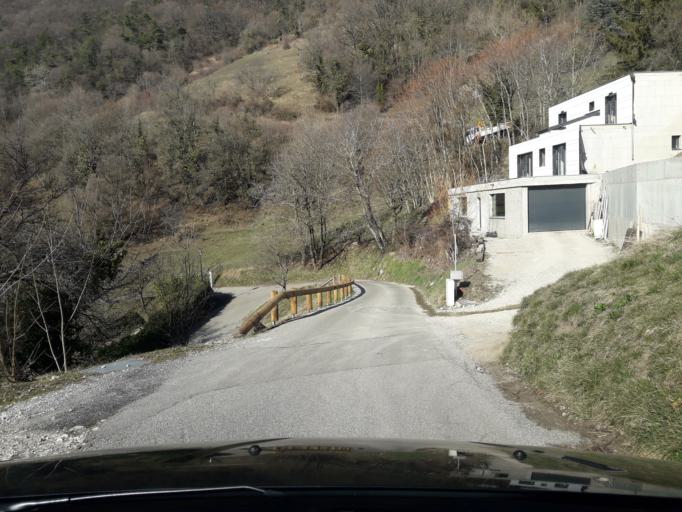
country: FR
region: Rhone-Alpes
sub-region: Departement de l'Isere
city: La Tronche
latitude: 45.2216
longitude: 5.7476
